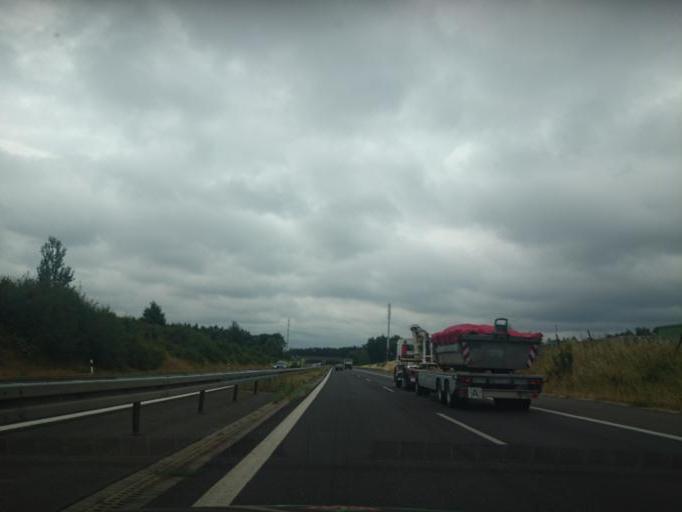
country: DE
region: Brandenburg
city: Grossbeeren
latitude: 52.3391
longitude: 13.2826
